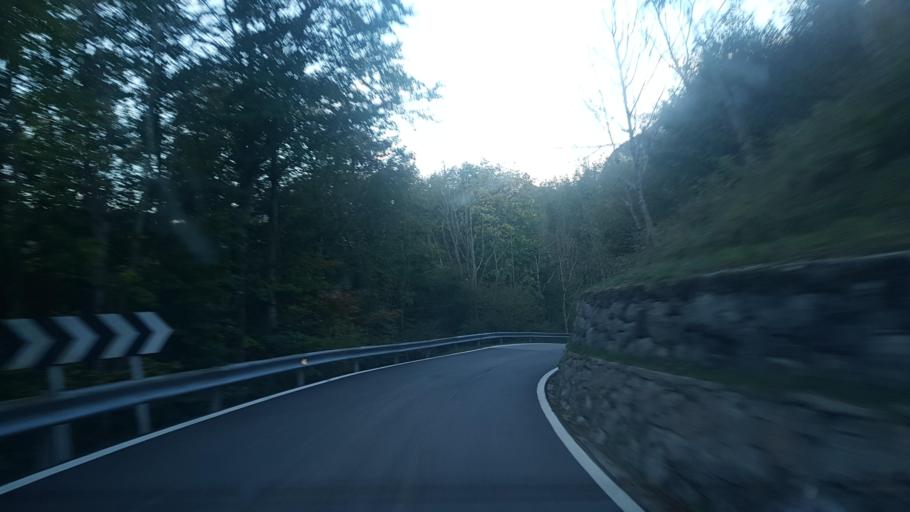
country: IT
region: Friuli Venezia Giulia
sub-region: Provincia di Udine
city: Villa Santina
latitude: 46.3525
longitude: 12.9270
